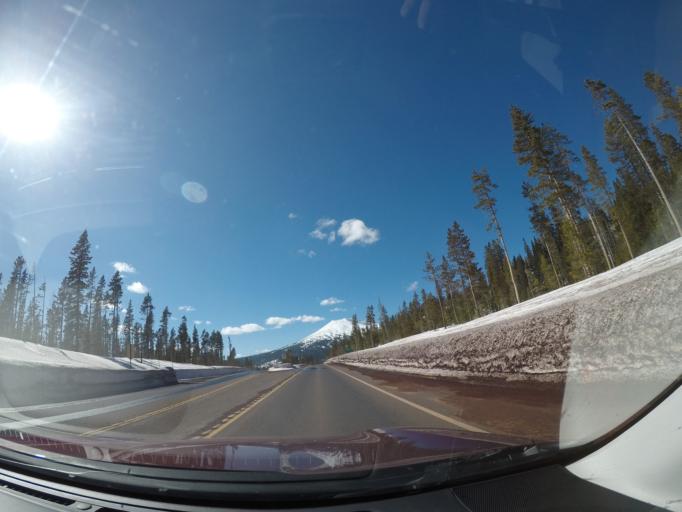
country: US
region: Oregon
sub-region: Deschutes County
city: Sunriver
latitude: 43.9833
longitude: -121.6078
